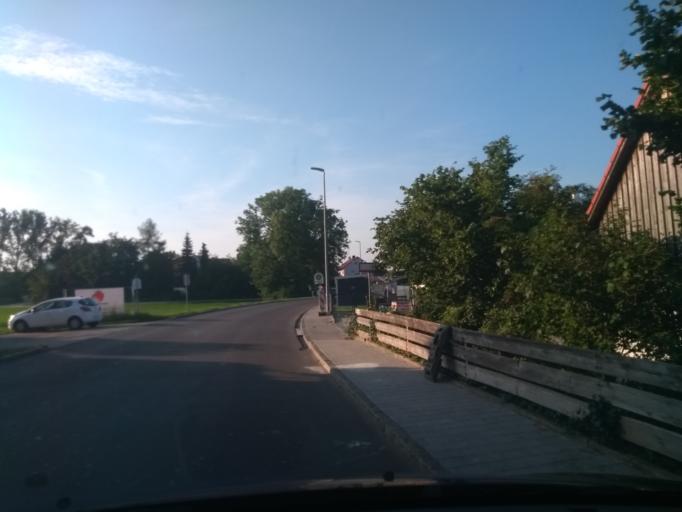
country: DE
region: Bavaria
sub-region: Upper Bavaria
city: Schwabhausen
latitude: 48.3798
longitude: 11.3537
